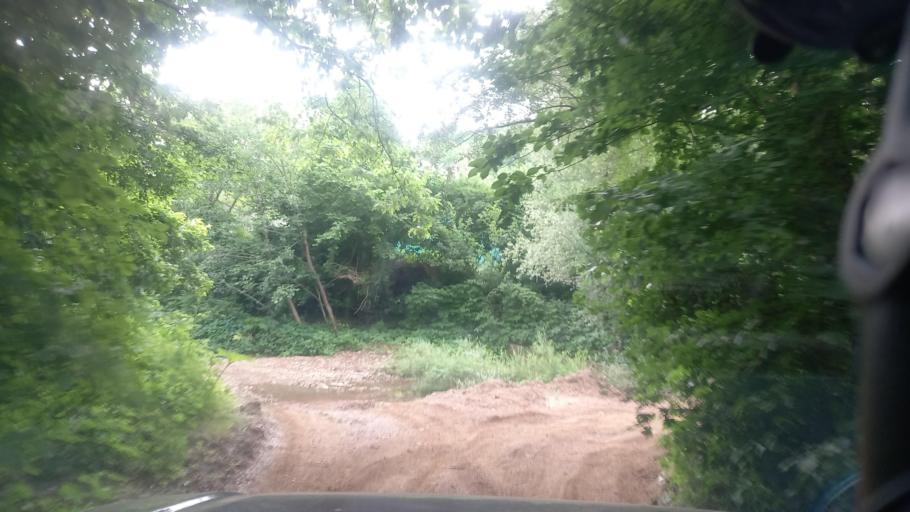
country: RU
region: Krasnodarskiy
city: Goryachiy Klyuch
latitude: 44.6099
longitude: 39.0335
